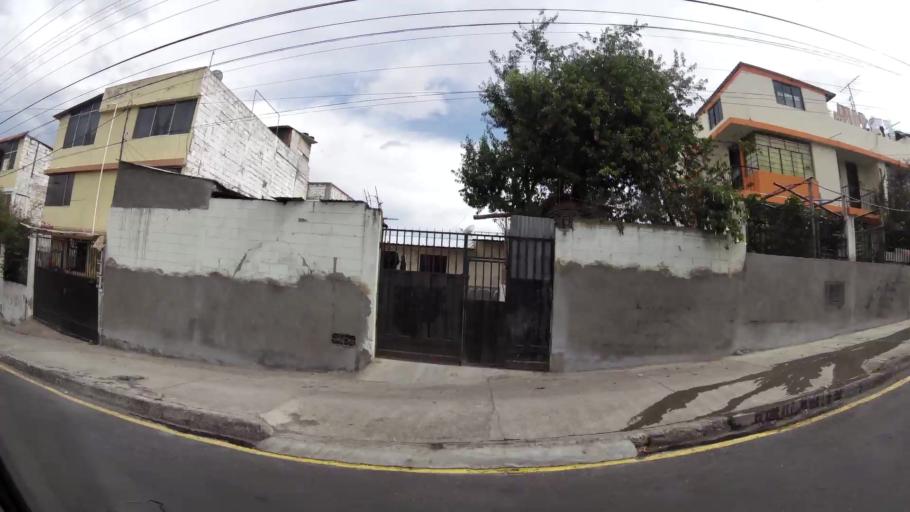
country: EC
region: Tungurahua
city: Ambato
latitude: -1.2683
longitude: -78.6343
